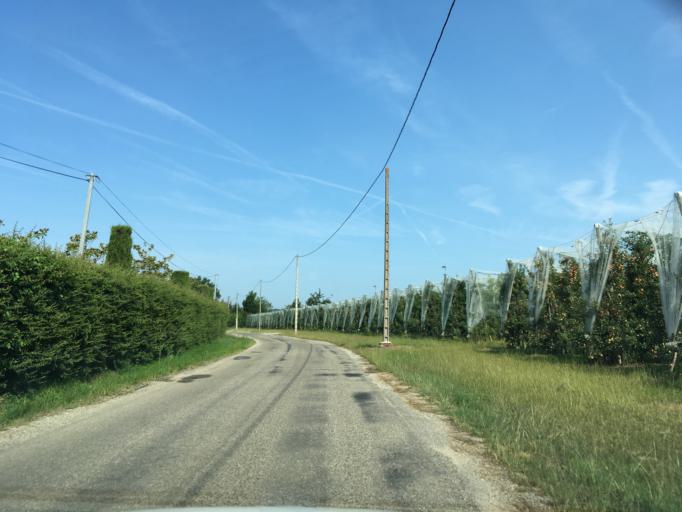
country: FR
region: Midi-Pyrenees
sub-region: Departement du Tarn-et-Garonne
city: Albias
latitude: 44.0676
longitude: 1.4174
